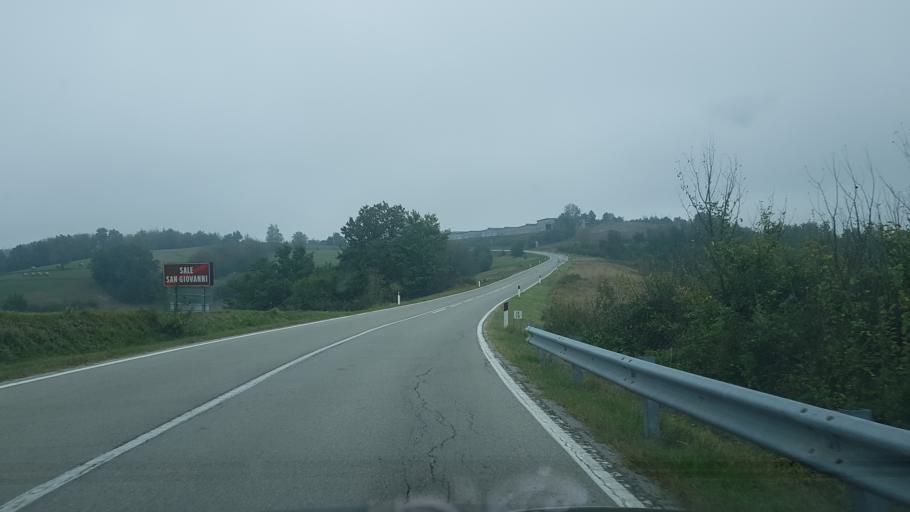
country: IT
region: Piedmont
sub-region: Provincia di Cuneo
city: Sale San Giovanni
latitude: 44.4116
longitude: 8.0927
